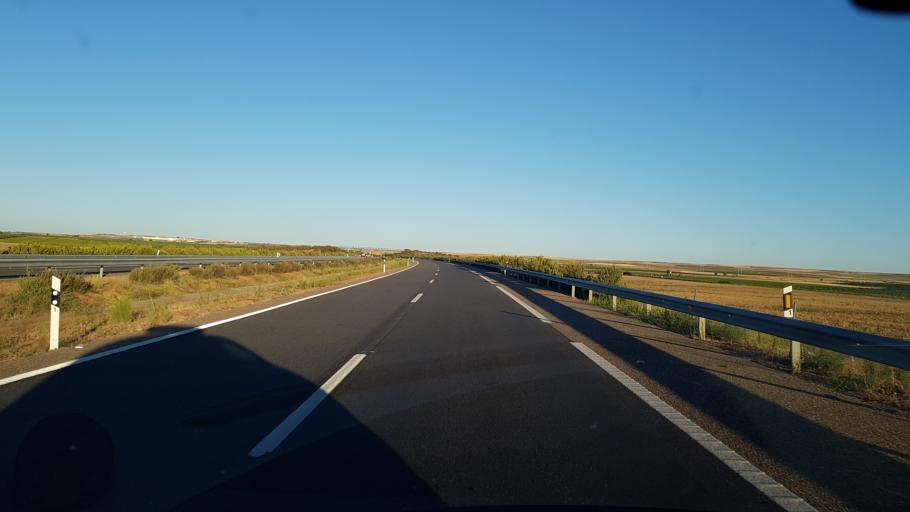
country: ES
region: Castille and Leon
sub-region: Provincia de Zamora
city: Morales de Toro
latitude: 41.5453
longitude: -5.3078
